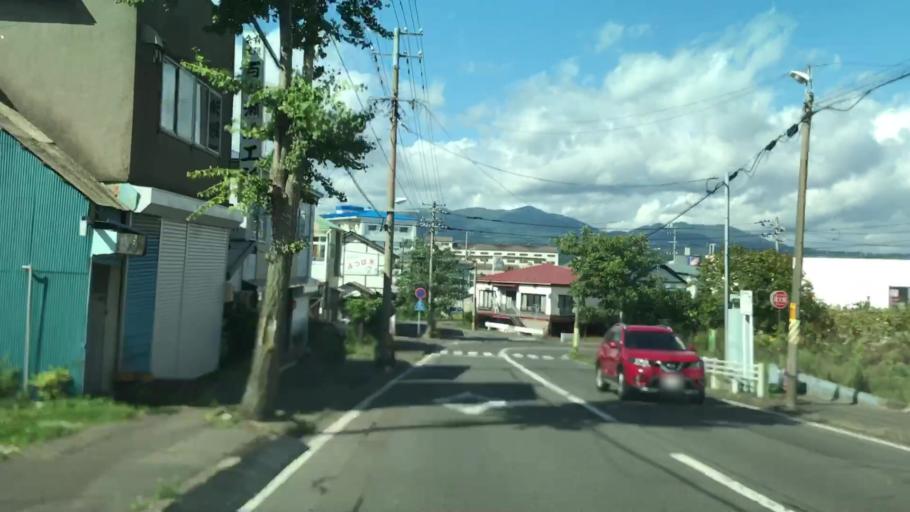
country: JP
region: Hokkaido
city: Muroran
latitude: 42.3264
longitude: 140.9674
